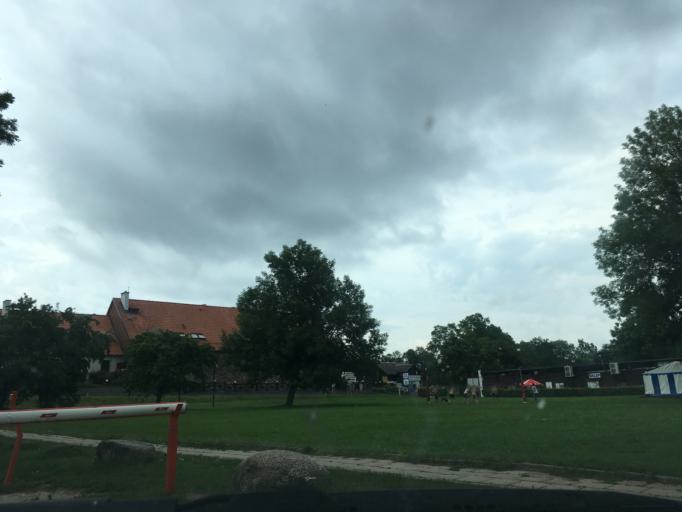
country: PL
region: Warmian-Masurian Voivodeship
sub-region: Powiat wegorzewski
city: Wegorzewo
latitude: 54.1311
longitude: 21.6831
